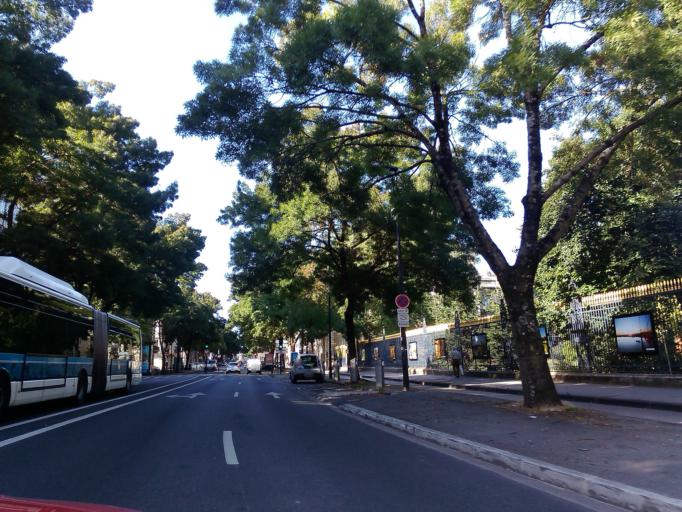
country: FR
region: Aquitaine
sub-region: Departement de la Gironde
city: Bordeaux
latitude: 44.8477
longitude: -0.5764
